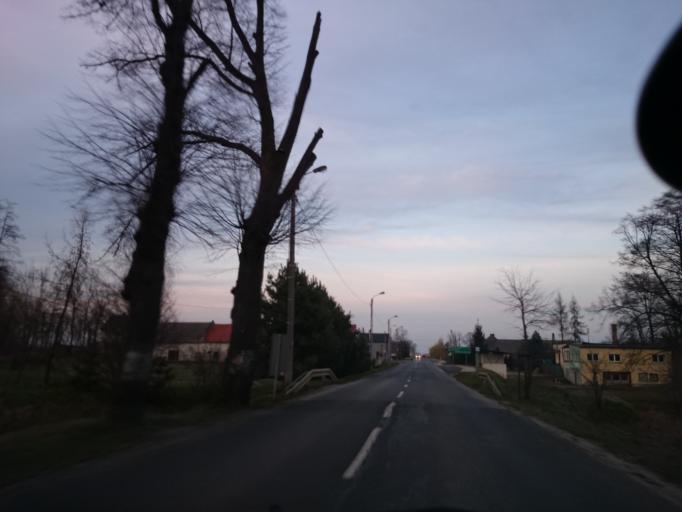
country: PL
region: Opole Voivodeship
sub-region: Powiat prudnicki
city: Lubrza
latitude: 50.3372
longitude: 17.6170
